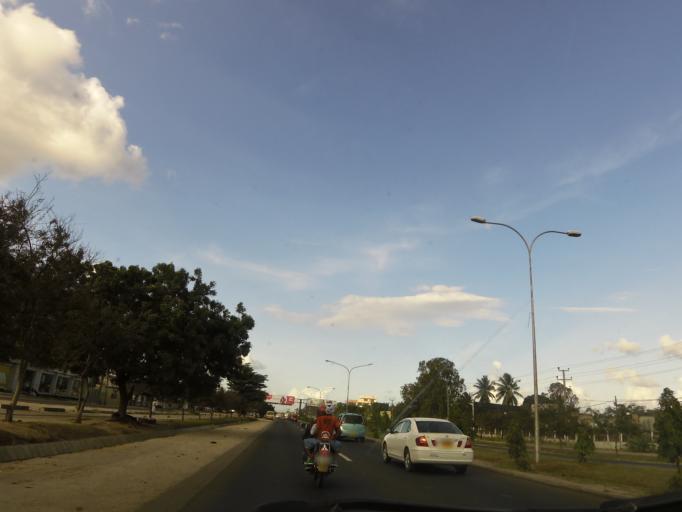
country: TZ
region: Dar es Salaam
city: Dar es Salaam
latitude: -6.8533
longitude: 39.2270
